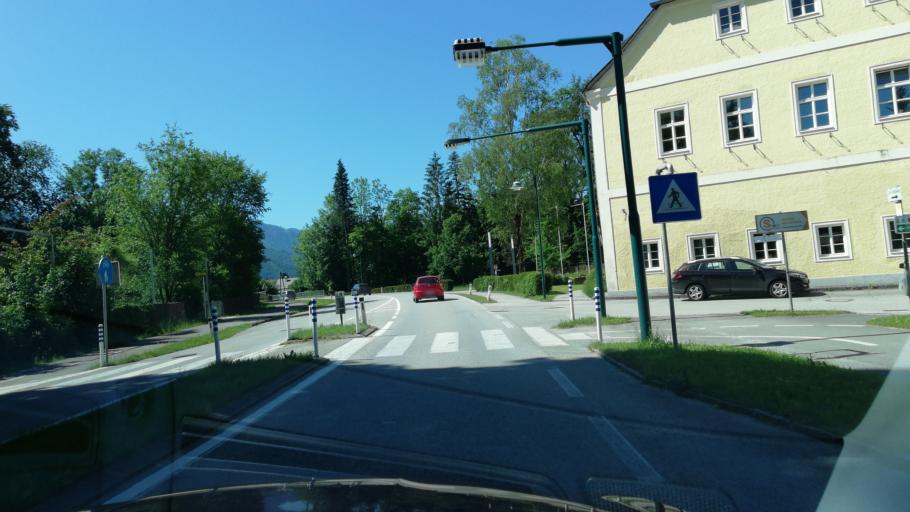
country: AT
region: Upper Austria
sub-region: Politischer Bezirk Kirchdorf an der Krems
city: Gruenburg
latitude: 47.9083
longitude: 14.2355
